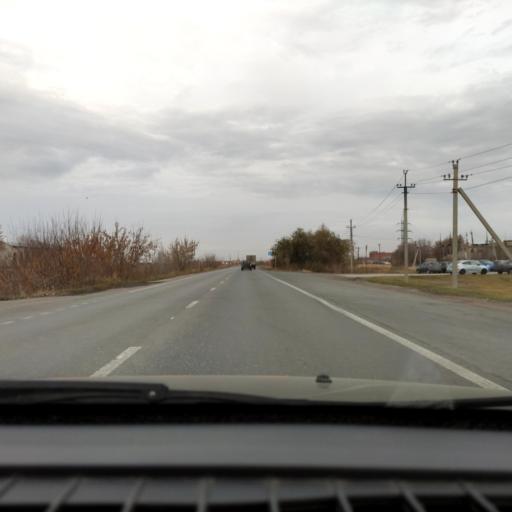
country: RU
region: Samara
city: Tol'yatti
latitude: 53.5678
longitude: 49.3475
